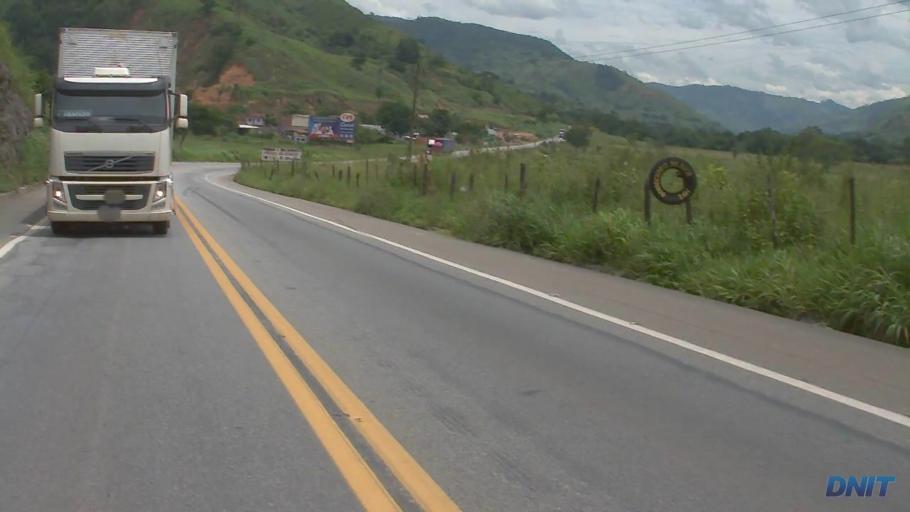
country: BR
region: Minas Gerais
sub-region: Timoteo
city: Timoteo
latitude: -19.5994
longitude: -42.7510
